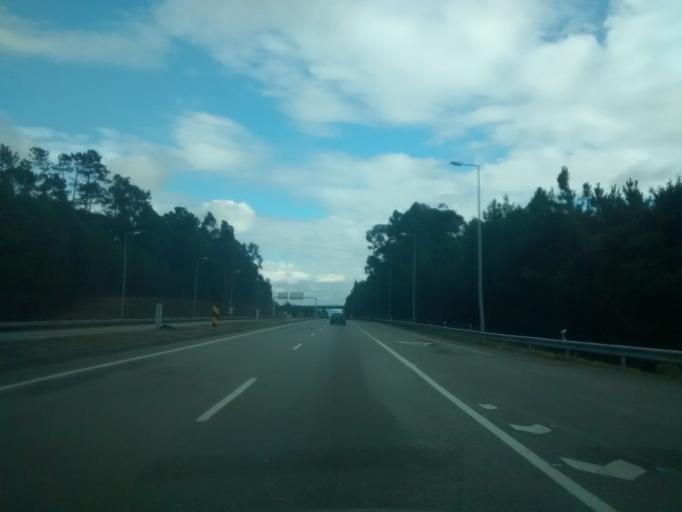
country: PT
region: Aveiro
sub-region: Agueda
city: Agueda
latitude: 40.5531
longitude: -8.4734
